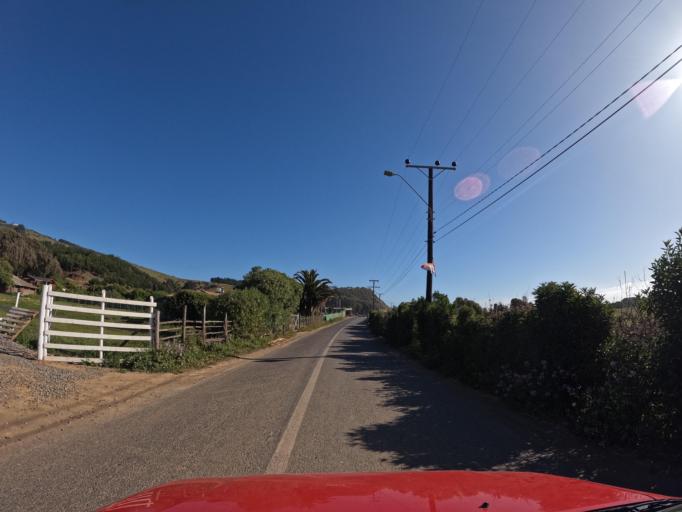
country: CL
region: Maule
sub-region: Provincia de Talca
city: Constitucion
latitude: -34.8527
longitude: -72.1419
